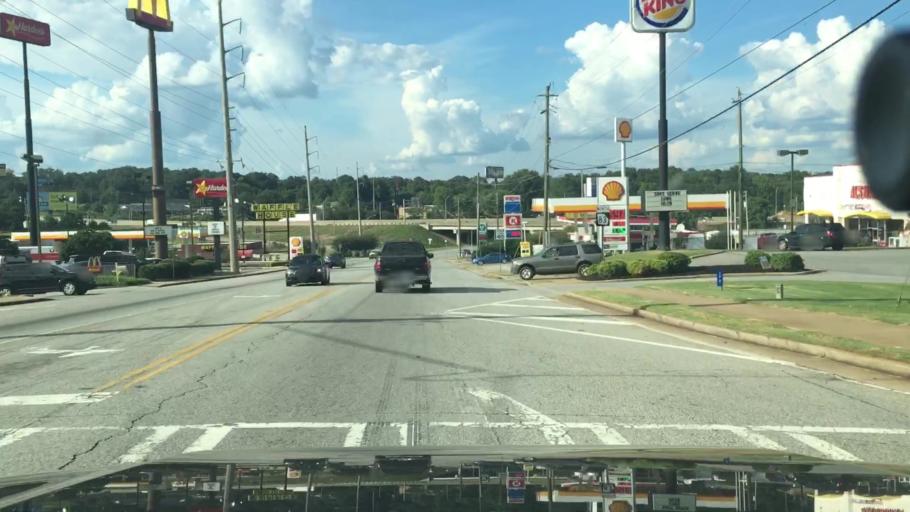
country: US
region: Georgia
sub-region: Monroe County
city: Forsyth
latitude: 33.0400
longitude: -83.9383
